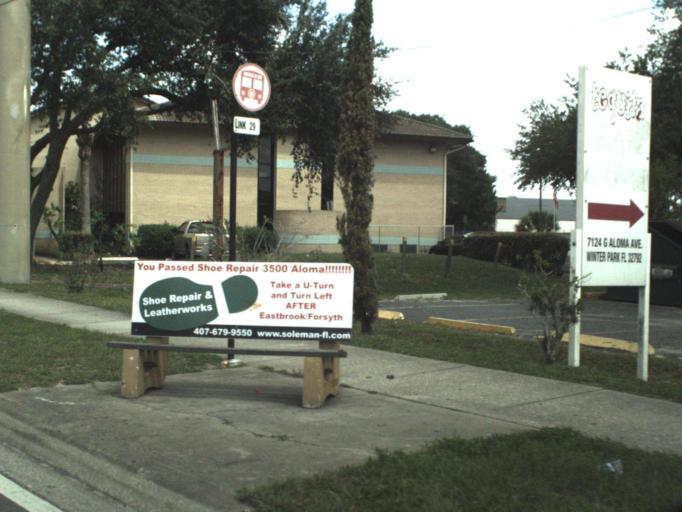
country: US
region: Florida
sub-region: Seminole County
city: Goldenrod
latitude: 28.6075
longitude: -81.2930
